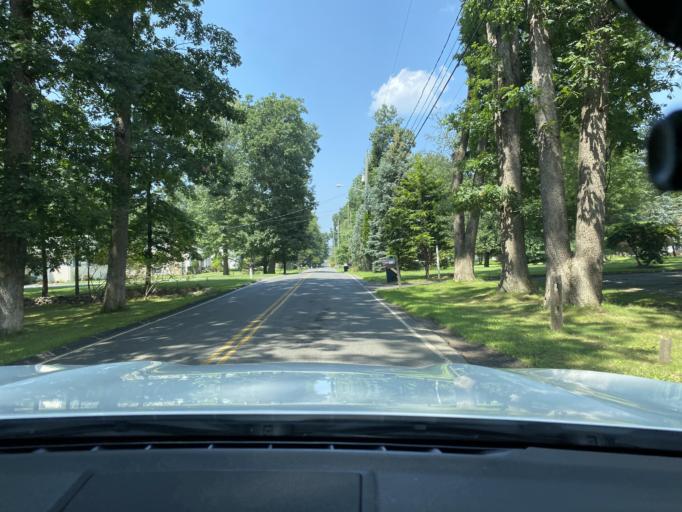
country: US
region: New York
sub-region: Rockland County
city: Airmont
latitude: 41.0926
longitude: -74.1123
